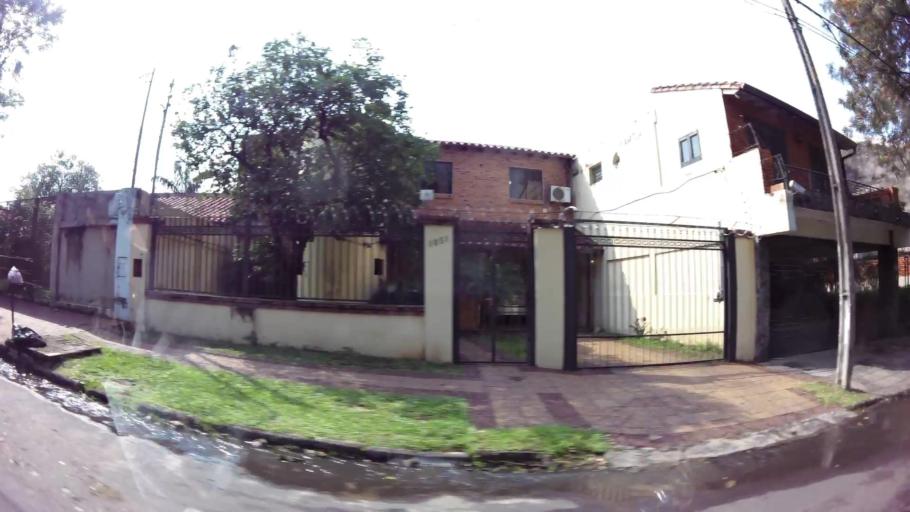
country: PY
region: Asuncion
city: Asuncion
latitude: -25.2958
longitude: -57.6600
